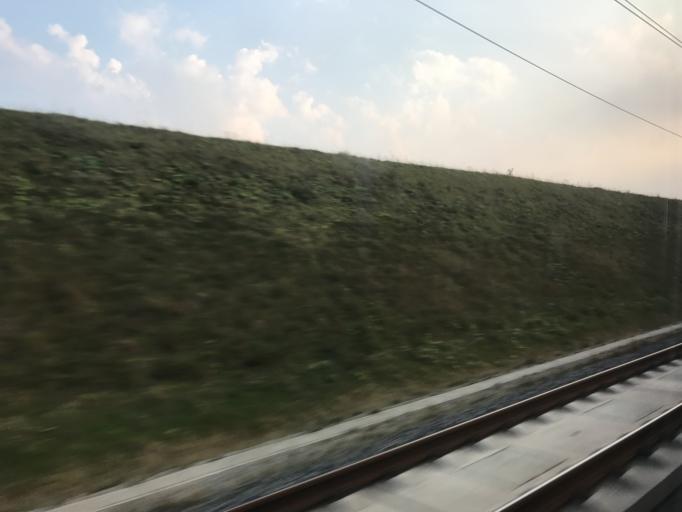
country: DE
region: Saxony-Anhalt
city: Holleben
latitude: 51.4021
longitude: 11.9233
